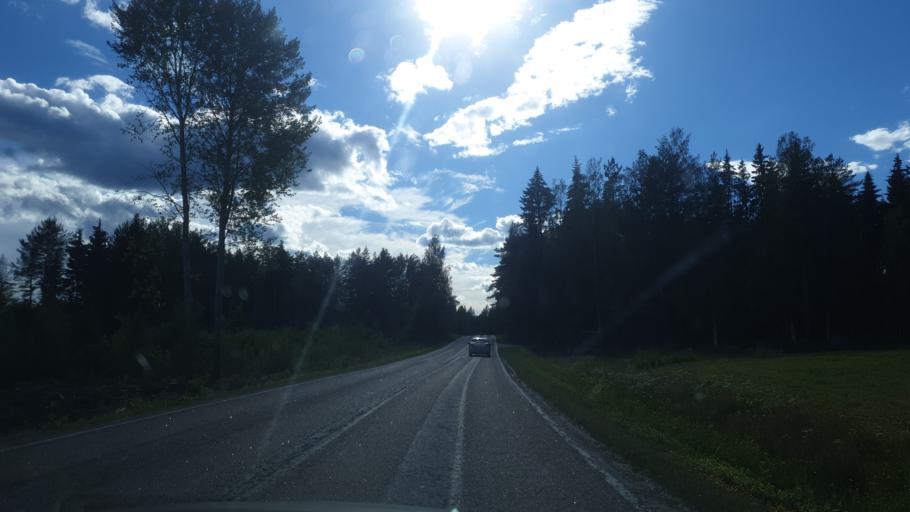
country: FI
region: Southern Savonia
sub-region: Mikkeli
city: Pertunmaa
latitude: 61.5242
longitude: 26.5946
